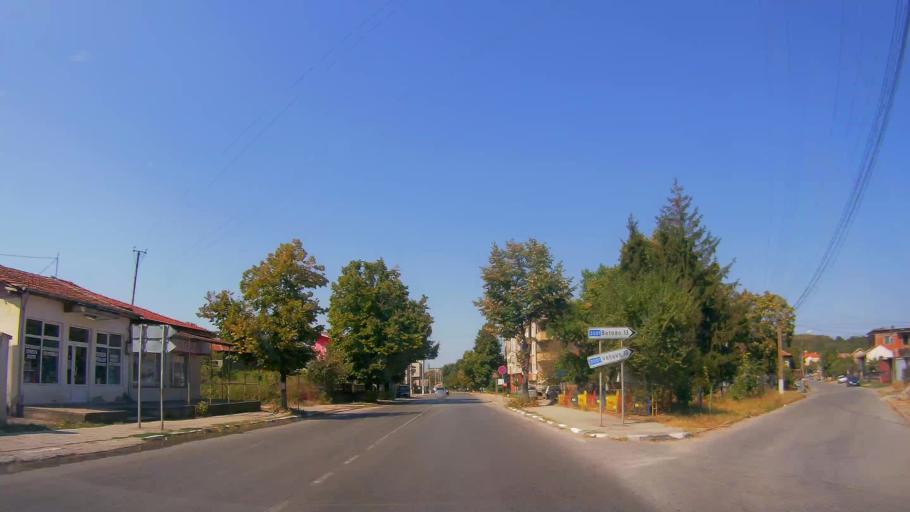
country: BG
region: Razgrad
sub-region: Obshtina Tsar Kaloyan
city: Tsar Kaloyan
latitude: 43.6070
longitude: 26.2392
